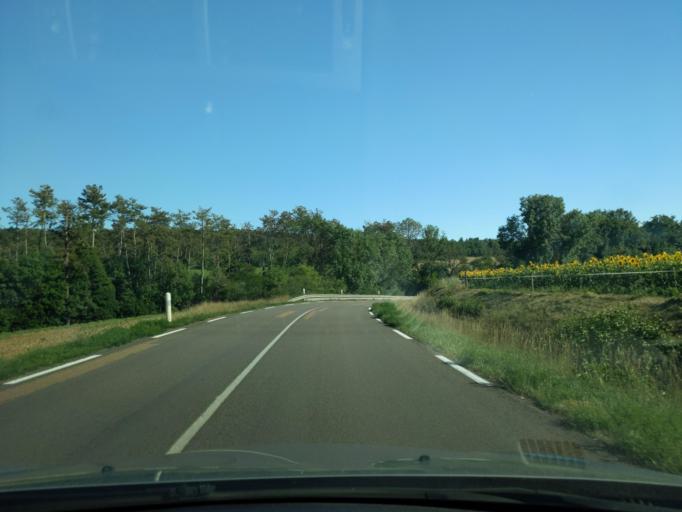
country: FR
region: Bourgogne
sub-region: Departement de la Cote-d'Or
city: Is-sur-Tille
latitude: 47.5115
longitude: 5.0751
